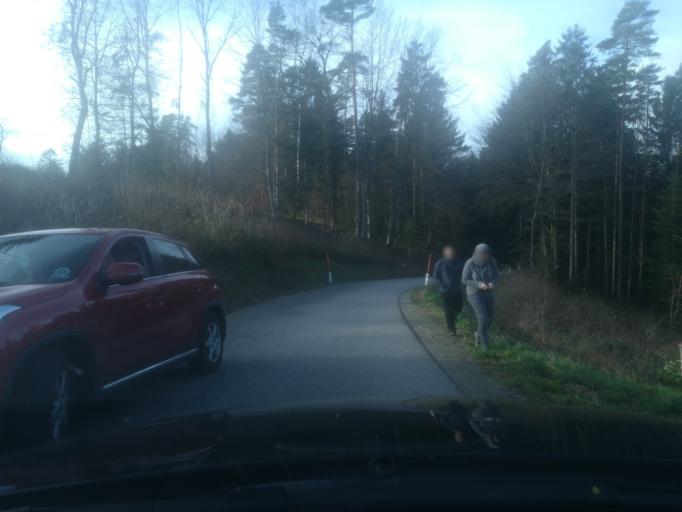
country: AT
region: Upper Austria
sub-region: Politischer Bezirk Perg
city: Perg
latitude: 48.3278
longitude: 14.6526
